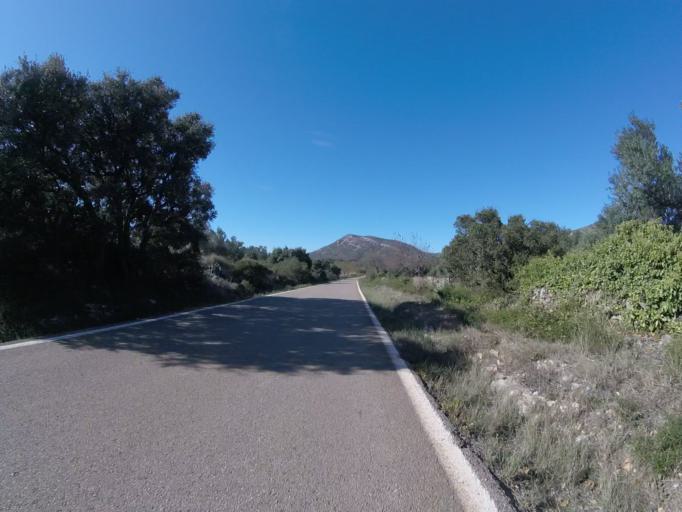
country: ES
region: Valencia
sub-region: Provincia de Castello
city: Cati
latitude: 40.4155
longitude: 0.0671
